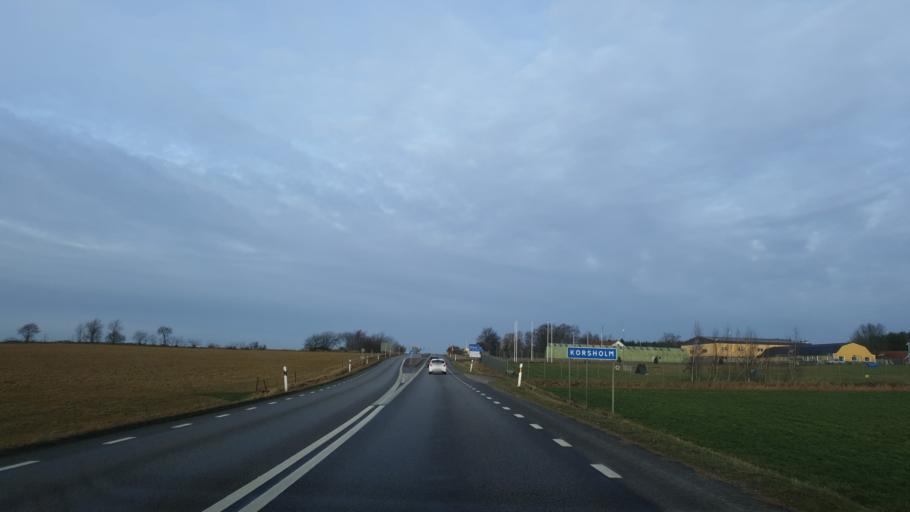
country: SE
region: Skane
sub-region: Horby Kommun
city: Hoerby
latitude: 55.7893
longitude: 13.6769
